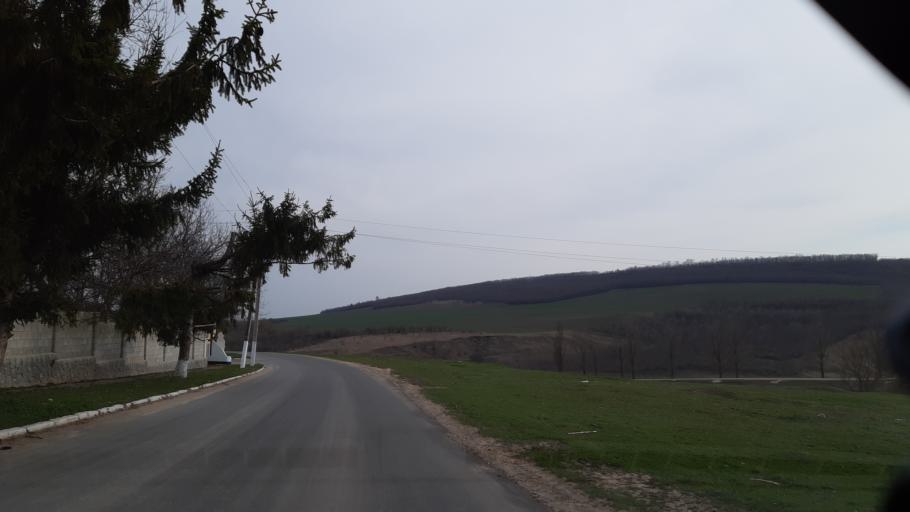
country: MD
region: Soldanesti
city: Soldanesti
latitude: 47.6817
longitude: 28.7812
